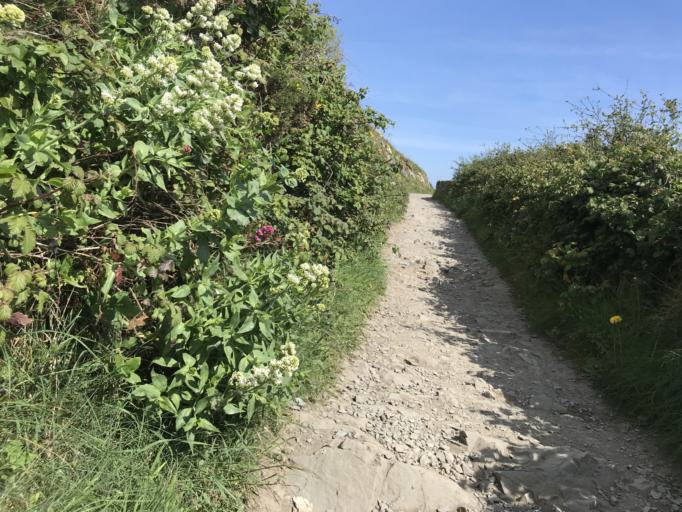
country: IE
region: Leinster
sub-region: Wicklow
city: Bray
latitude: 53.1854
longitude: -6.0778
